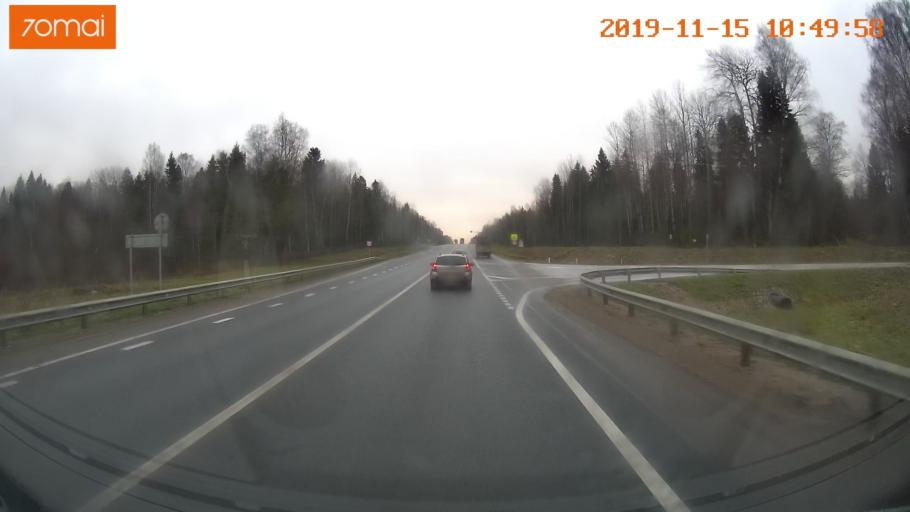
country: RU
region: Vologda
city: Sheksna
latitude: 59.1876
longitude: 38.6711
